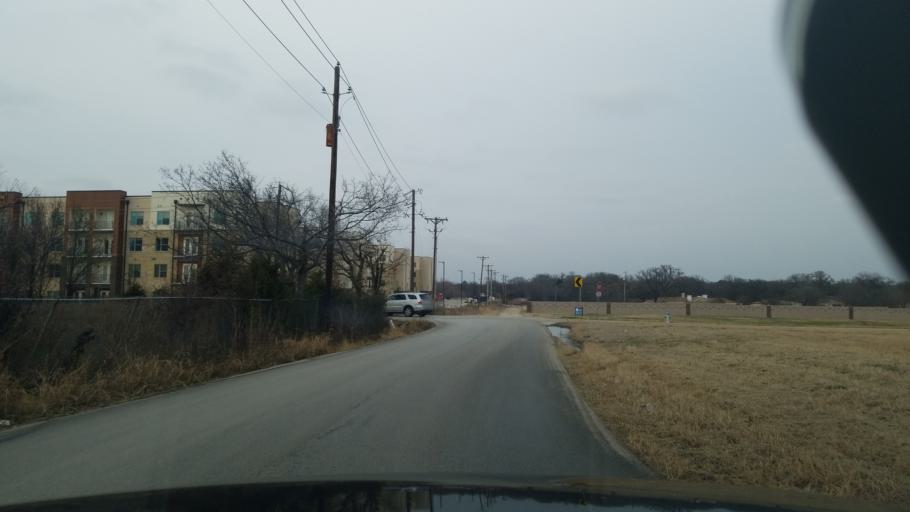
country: US
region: Texas
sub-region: Denton County
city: Corinth
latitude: 33.1447
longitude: -97.0512
